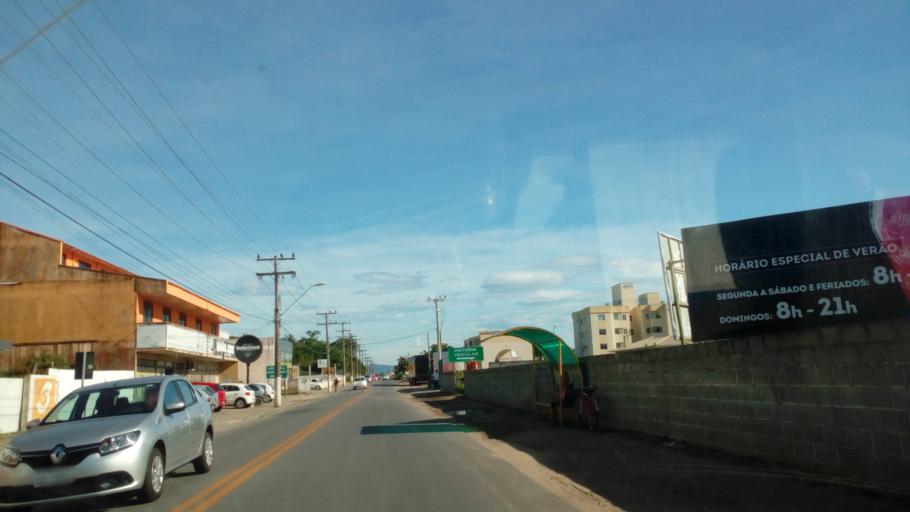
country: BR
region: Santa Catarina
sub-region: Laguna
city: Laguna
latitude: -28.4682
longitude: -48.7850
